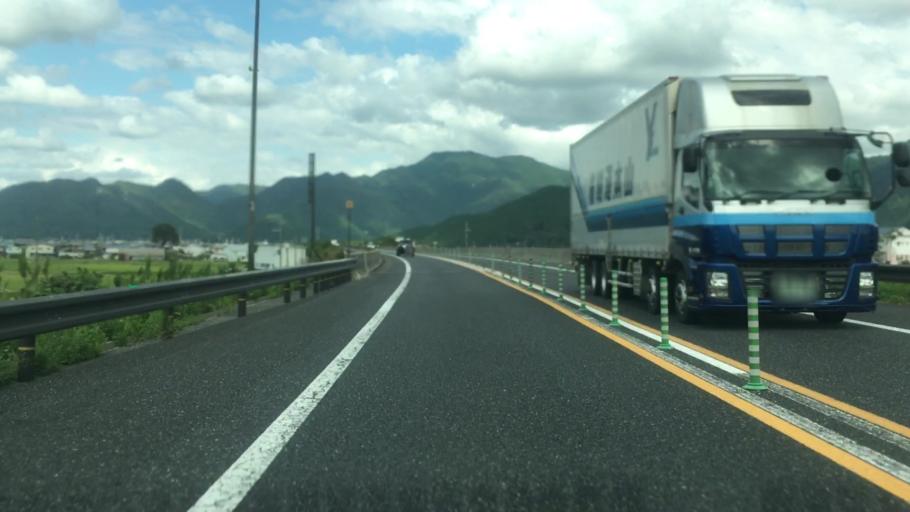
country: JP
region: Kyoto
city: Fukuchiyama
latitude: 35.1838
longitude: 135.0379
